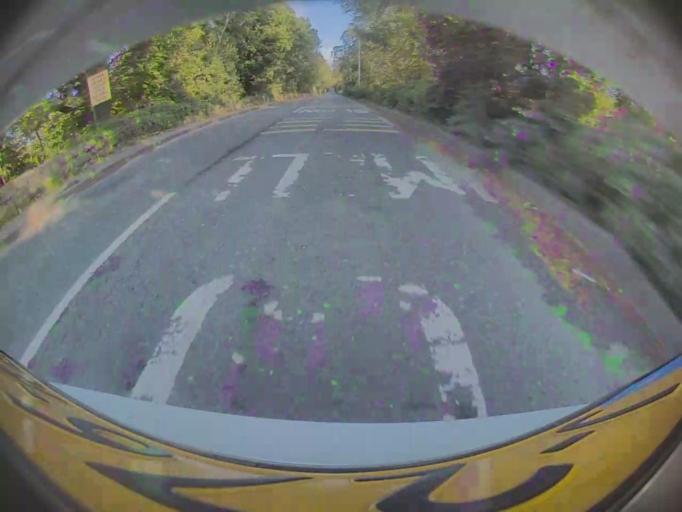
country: IE
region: Leinster
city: Foxrock
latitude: 53.2306
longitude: -6.1873
